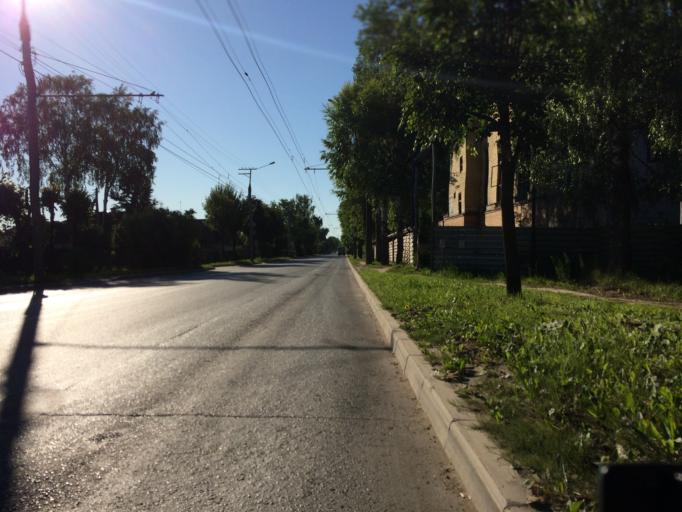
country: RU
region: Mariy-El
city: Yoshkar-Ola
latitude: 56.6517
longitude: 47.8869
